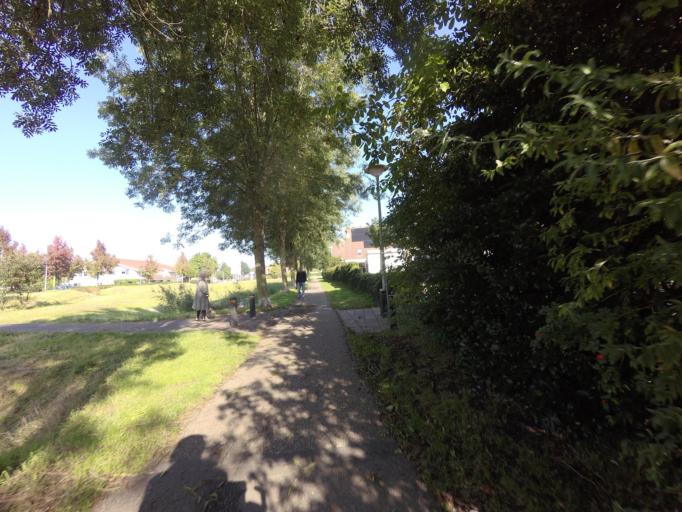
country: NL
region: Gelderland
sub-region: Gemeente Culemborg
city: Culemborg
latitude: 51.9486
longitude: 5.2071
